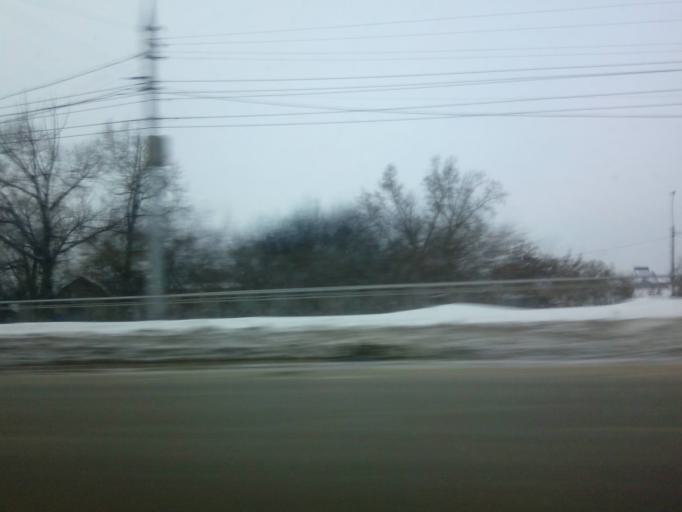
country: RU
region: Novosibirsk
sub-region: Novosibirskiy Rayon
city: Novosibirsk
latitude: 55.0133
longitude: 82.8801
